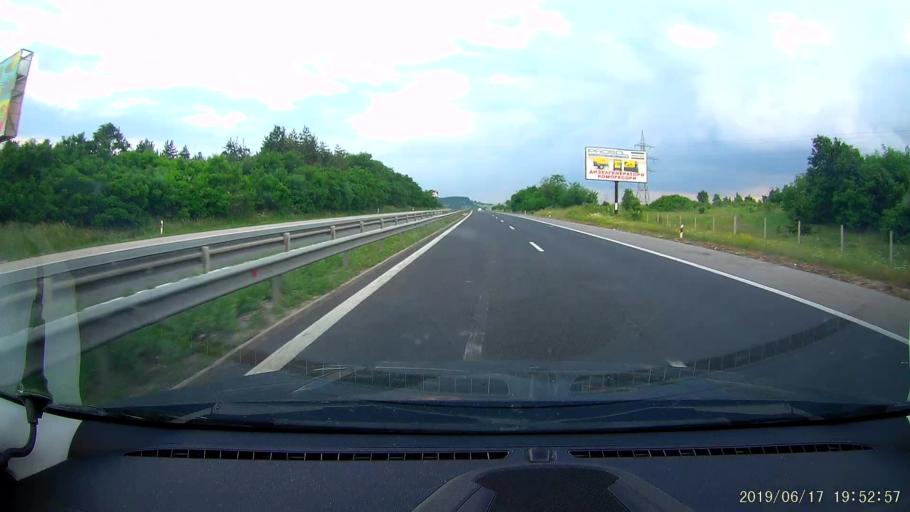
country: BG
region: Sofiya
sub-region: Obshtina Ikhtiman
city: Ikhtiman
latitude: 42.5341
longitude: 23.7326
